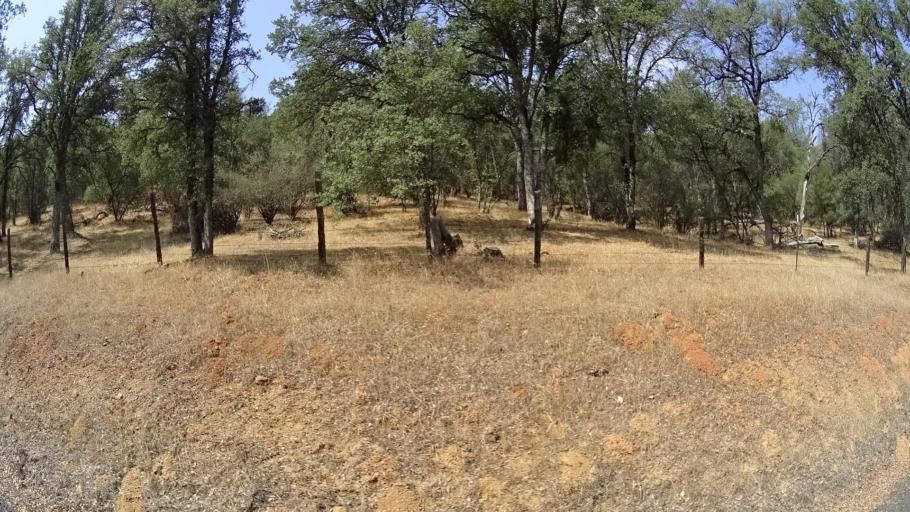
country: US
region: California
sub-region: Tuolumne County
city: Tuolumne City
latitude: 37.7136
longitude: -120.1816
